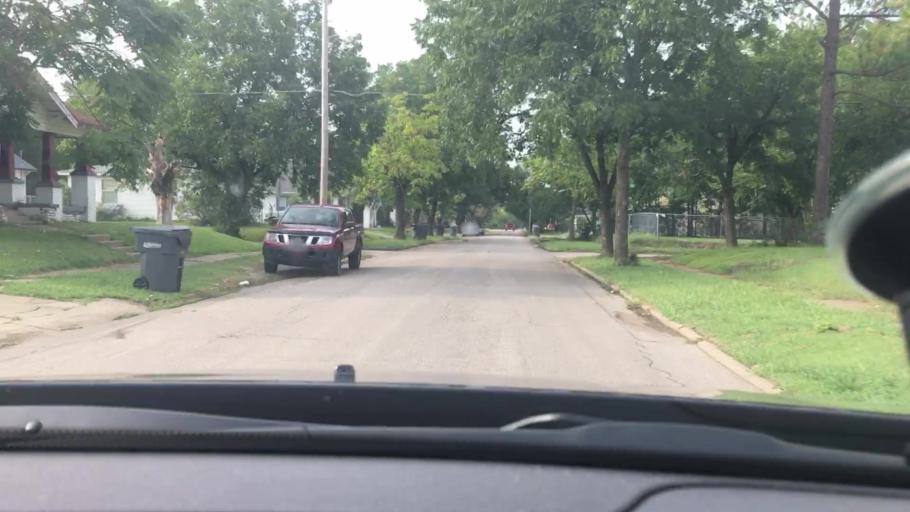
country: US
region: Oklahoma
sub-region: Carter County
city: Ardmore
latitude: 34.1800
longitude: -97.1288
